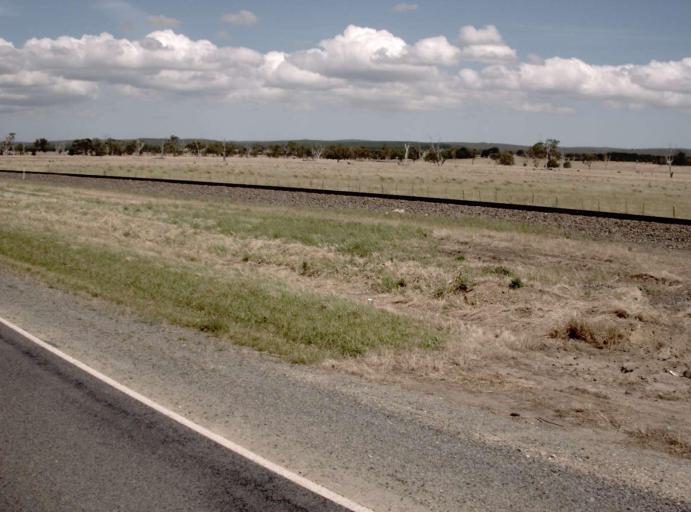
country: AU
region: Victoria
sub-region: Wellington
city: Heyfield
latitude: -38.1547
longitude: 146.8176
